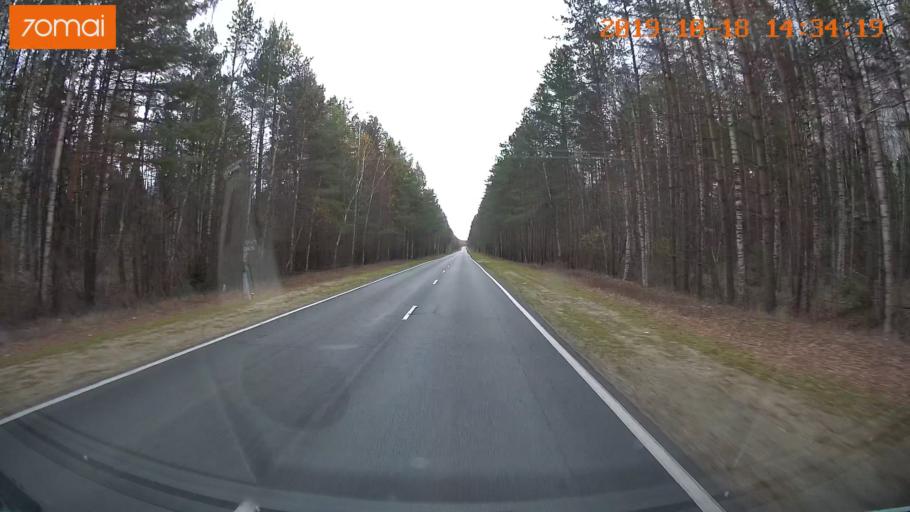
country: RU
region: Vladimir
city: Velikodvorskiy
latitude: 55.2109
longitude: 40.6138
